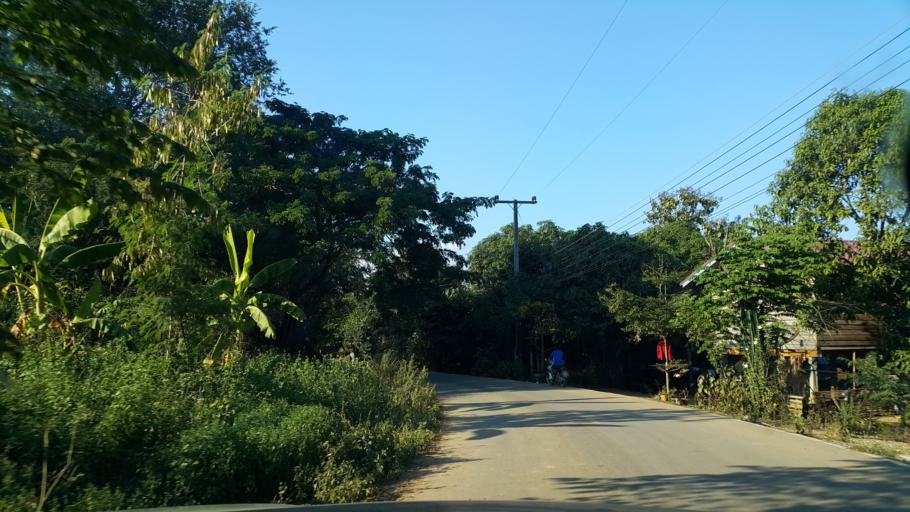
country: TH
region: Sukhothai
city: Thung Saliam
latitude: 17.4095
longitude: 99.5146
